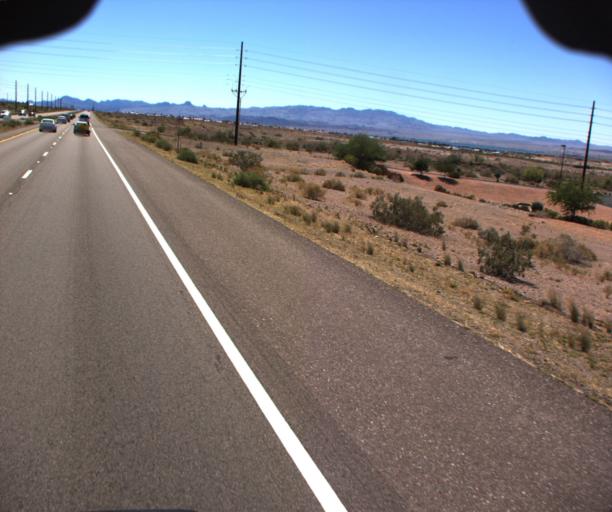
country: US
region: Arizona
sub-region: Mohave County
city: Desert Hills
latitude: 34.5621
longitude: -114.3610
